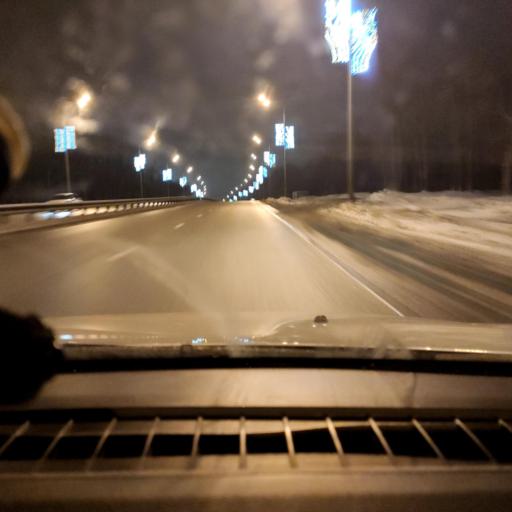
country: RU
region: Samara
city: Novosemeykino
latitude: 53.3205
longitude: 50.2302
